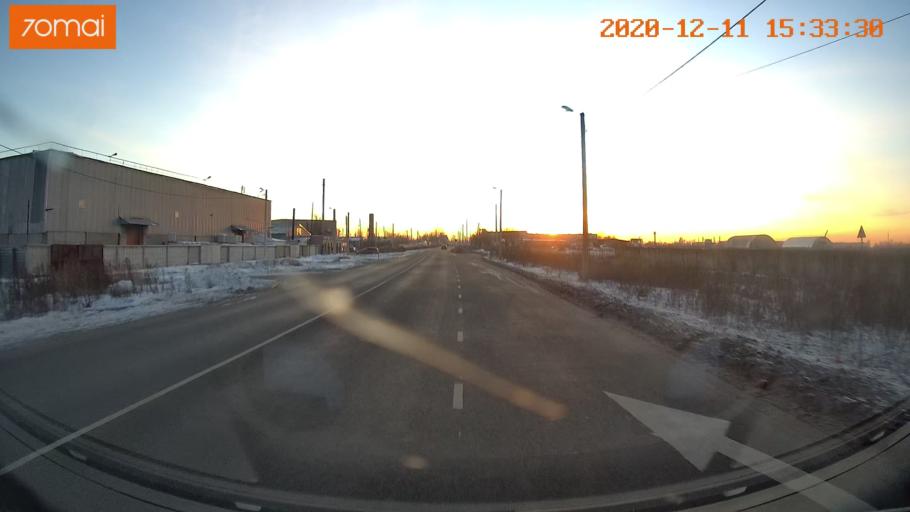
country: RU
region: Ivanovo
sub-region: Gorod Ivanovo
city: Ivanovo
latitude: 57.0521
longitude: 40.9473
